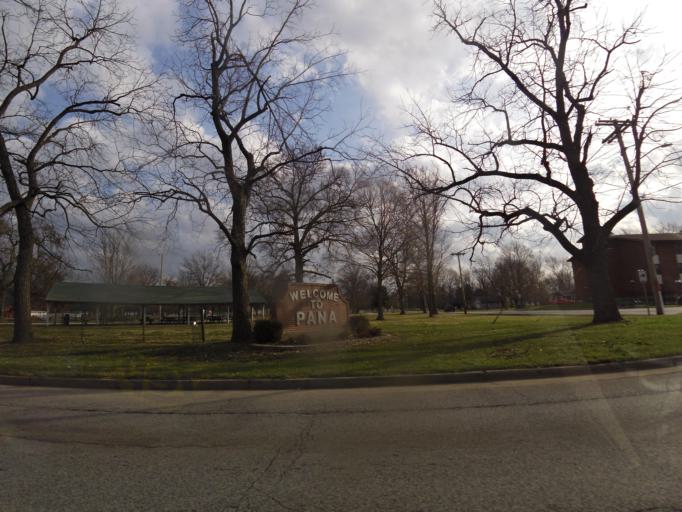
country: US
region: Illinois
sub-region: Christian County
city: Pana
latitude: 39.3762
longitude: -89.0817
